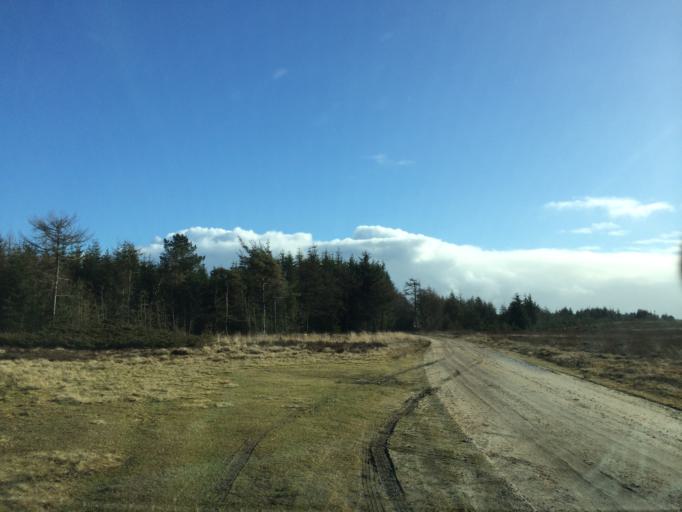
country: DK
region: Central Jutland
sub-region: Holstebro Kommune
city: Ulfborg
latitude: 56.2678
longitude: 8.4067
